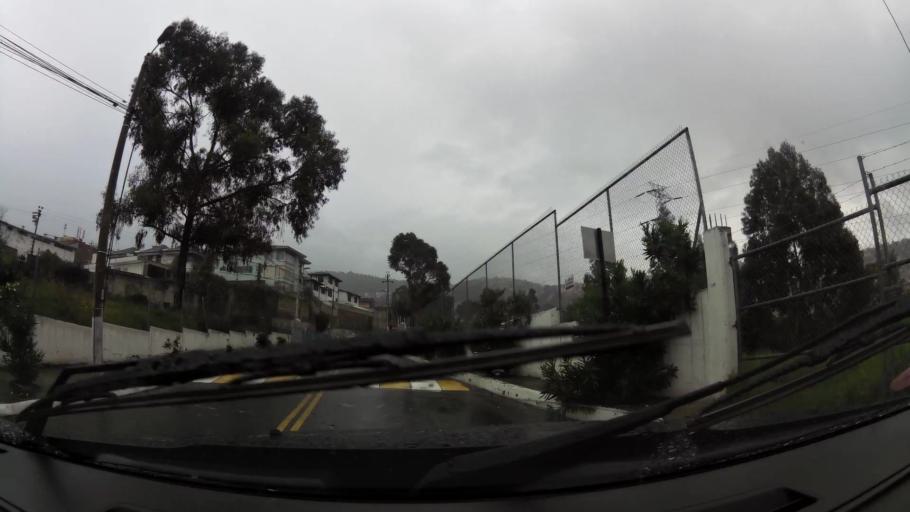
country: EC
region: Pichincha
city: Quito
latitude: -0.1011
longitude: -78.5039
